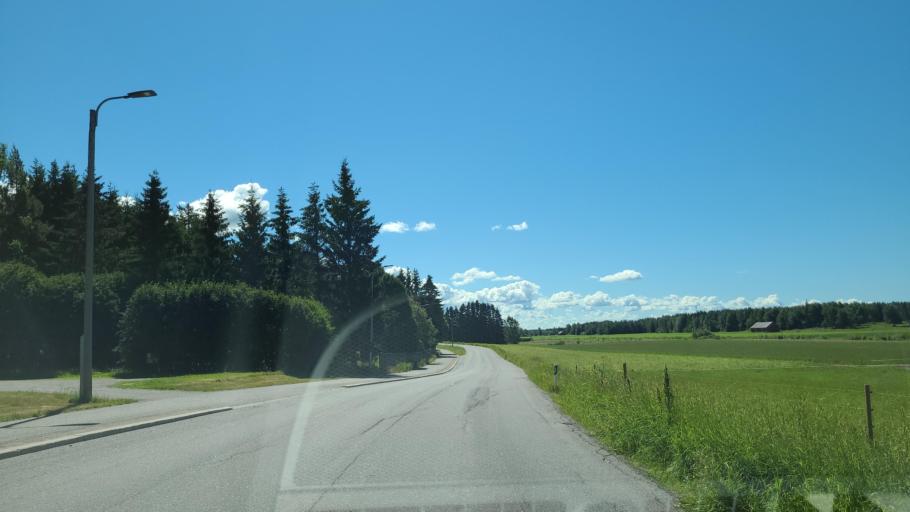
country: FI
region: Ostrobothnia
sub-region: Vaasa
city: Ristinummi
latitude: 63.0647
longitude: 21.7254
